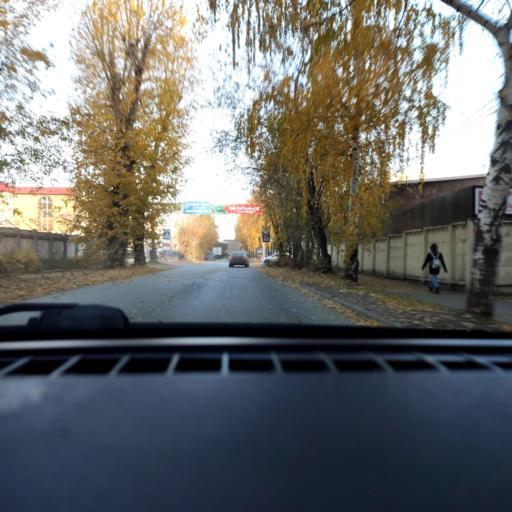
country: RU
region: Perm
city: Perm
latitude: 58.0103
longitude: 56.1824
